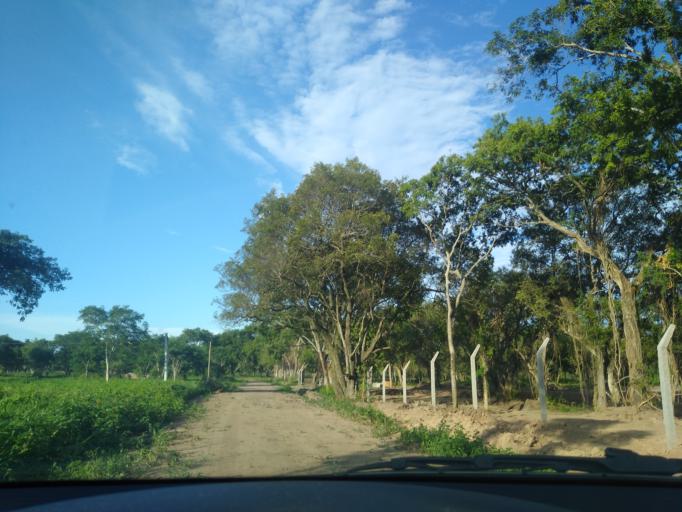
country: AR
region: Chaco
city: Resistencia
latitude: -27.4423
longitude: -58.9525
